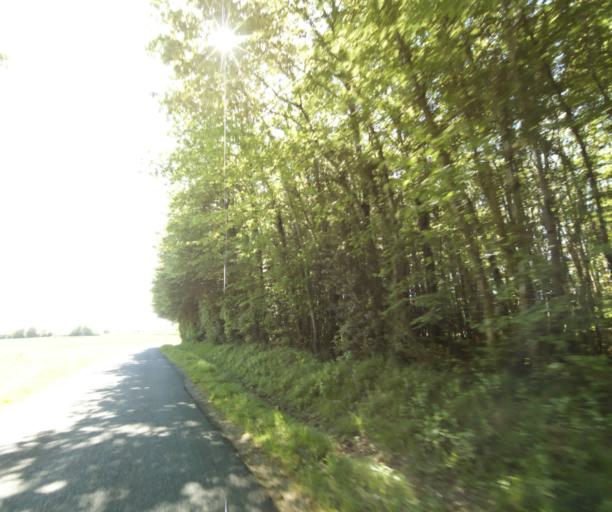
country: FR
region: Poitou-Charentes
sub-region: Departement de la Charente-Maritime
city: Bussac-sur-Charente
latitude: 45.8011
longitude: -0.6703
